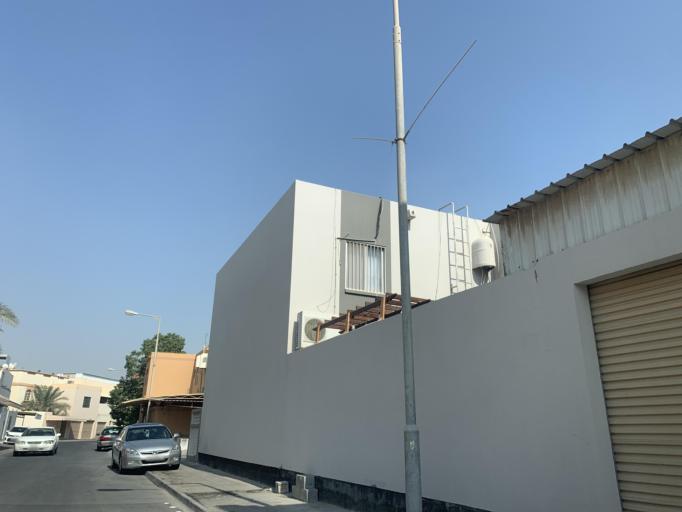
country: BH
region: Central Governorate
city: Madinat Hamad
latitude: 26.1218
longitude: 50.4933
